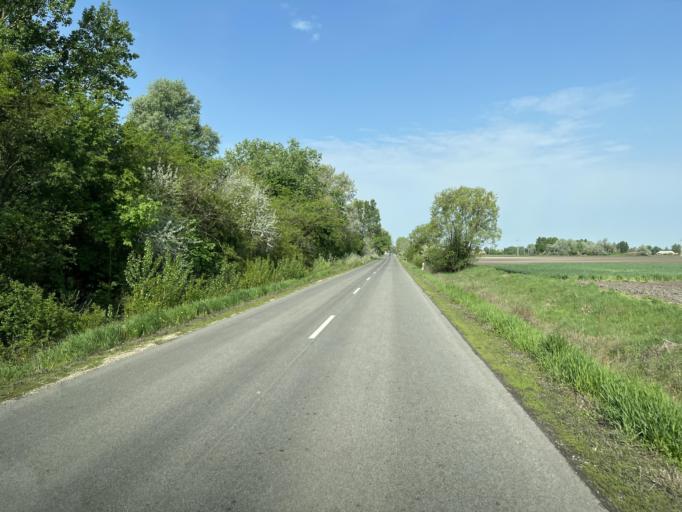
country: HU
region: Pest
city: Kocser
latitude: 46.9980
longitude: 19.9369
